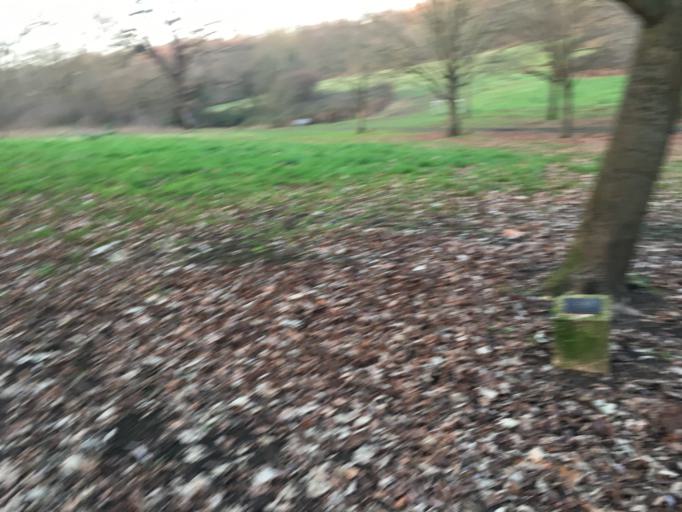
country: GB
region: England
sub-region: Greater London
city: Hendon
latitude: 51.6125
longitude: -0.2263
